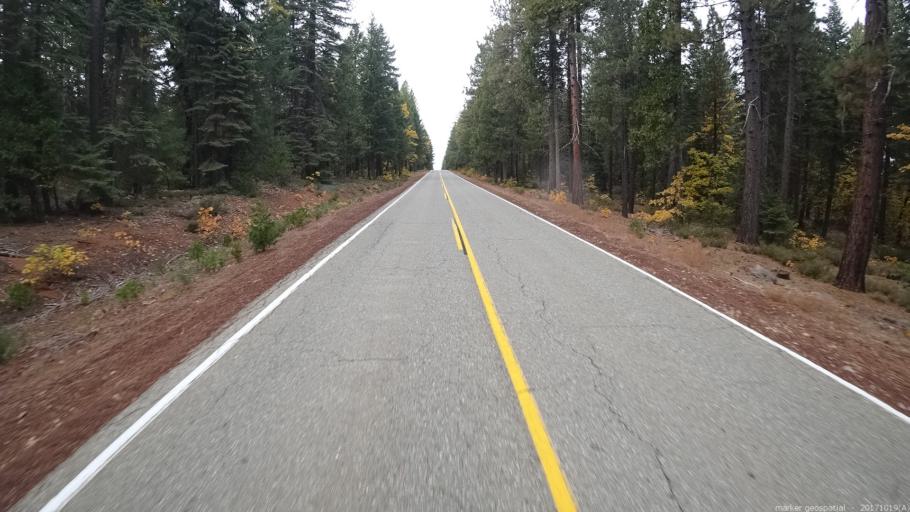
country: US
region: California
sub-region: Shasta County
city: Burney
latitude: 41.1382
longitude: -121.6214
